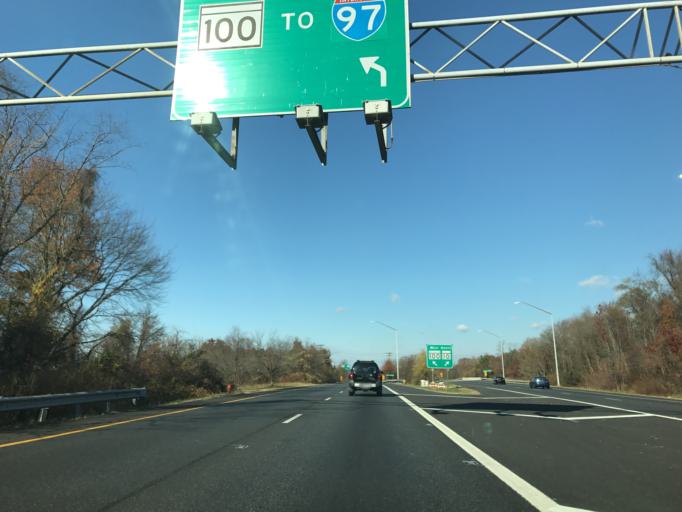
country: US
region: Maryland
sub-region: Anne Arundel County
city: Pasadena
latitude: 39.1304
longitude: -76.5833
